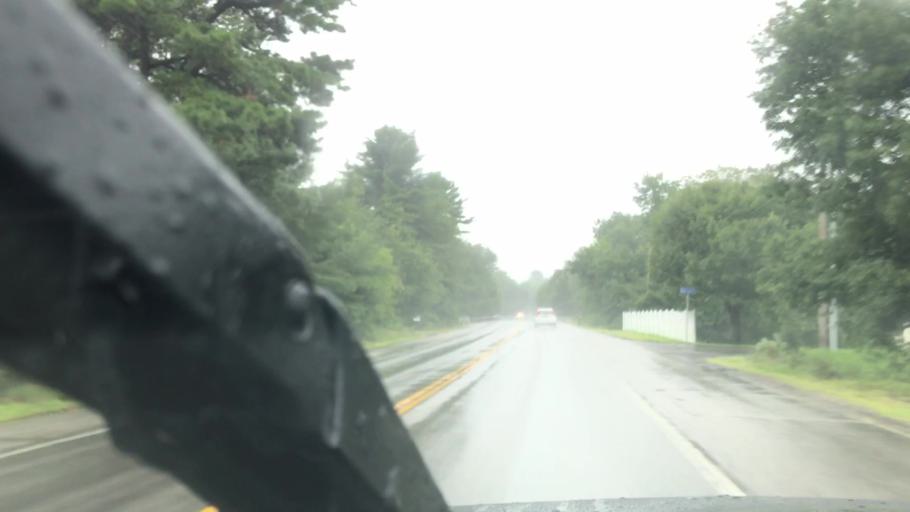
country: US
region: Maine
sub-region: York County
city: Wells Beach Station
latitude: 43.3143
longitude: -70.6522
